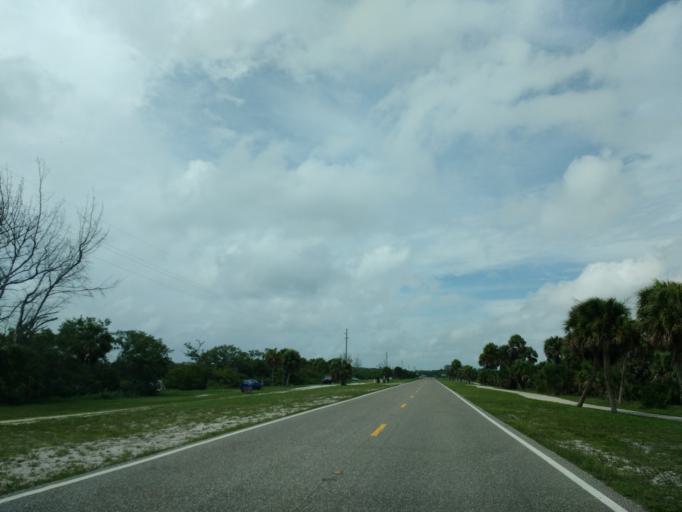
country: US
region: Florida
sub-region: Pinellas County
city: Tierra Verde
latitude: 27.6378
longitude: -82.7170
